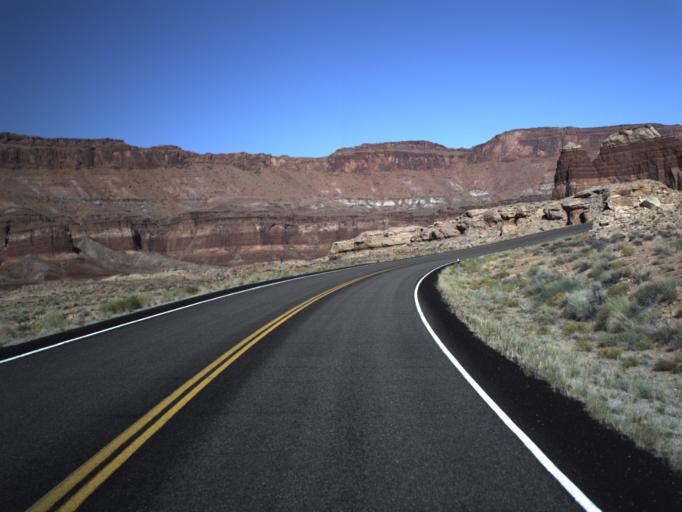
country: US
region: Utah
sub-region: San Juan County
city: Blanding
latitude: 37.8953
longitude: -110.3778
